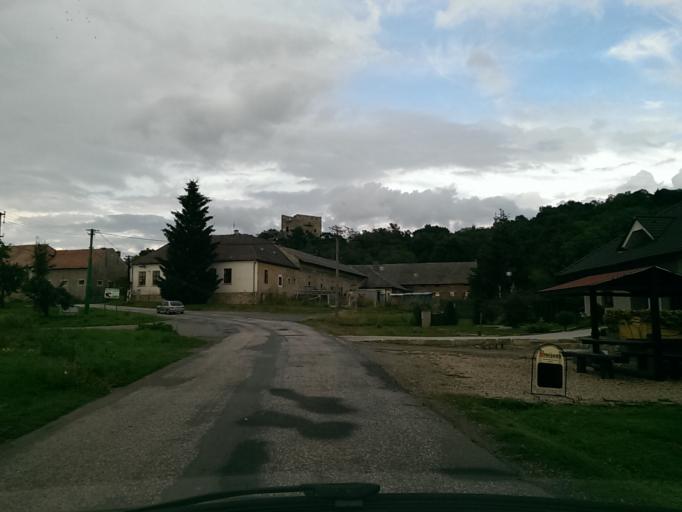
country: CZ
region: Central Bohemia
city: Knezmost
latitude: 50.5078
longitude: 15.0233
